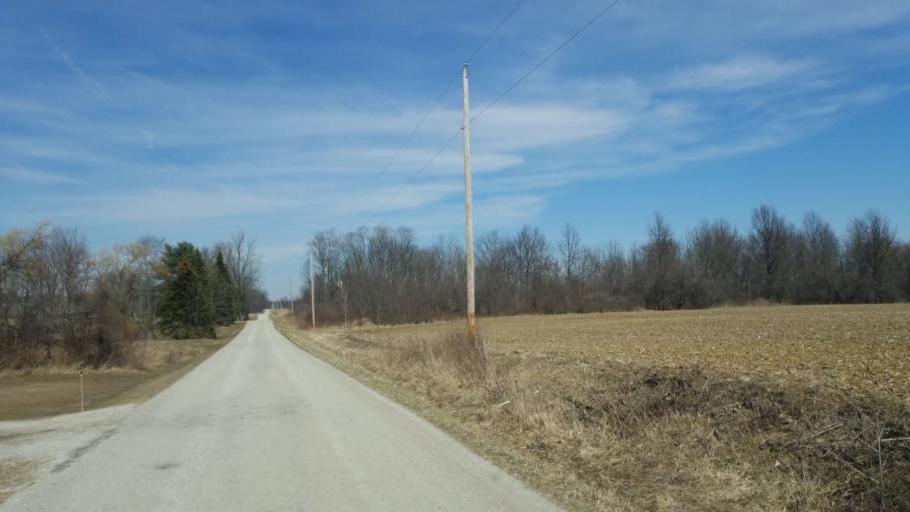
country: US
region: Ohio
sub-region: Crawford County
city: Galion
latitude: 40.6946
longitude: -82.7559
